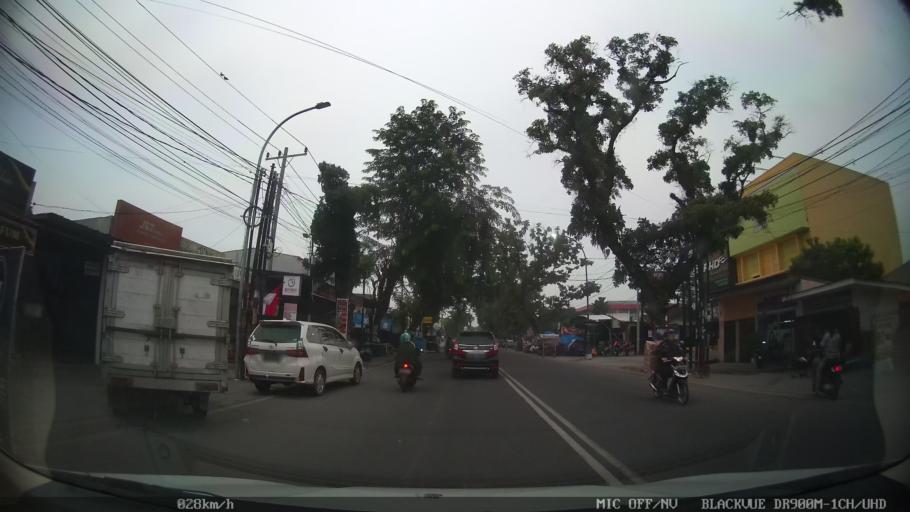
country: ID
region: North Sumatra
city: Medan
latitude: 3.5686
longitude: 98.7000
